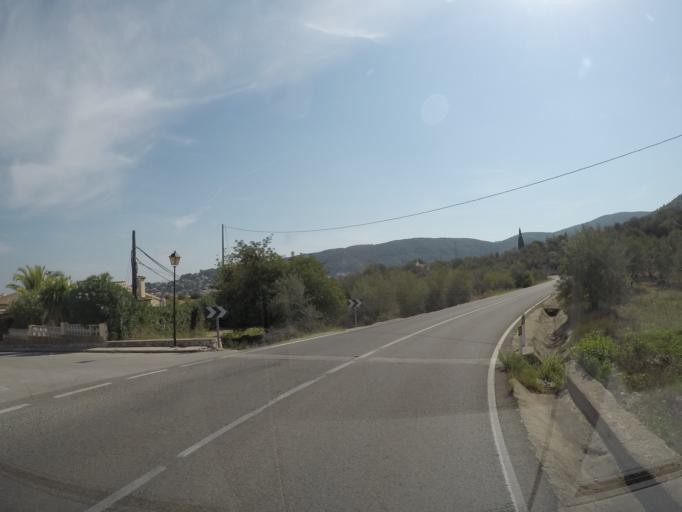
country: ES
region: Valencia
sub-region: Provincia de Alicante
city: Orba
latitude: 38.7802
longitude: -0.0712
